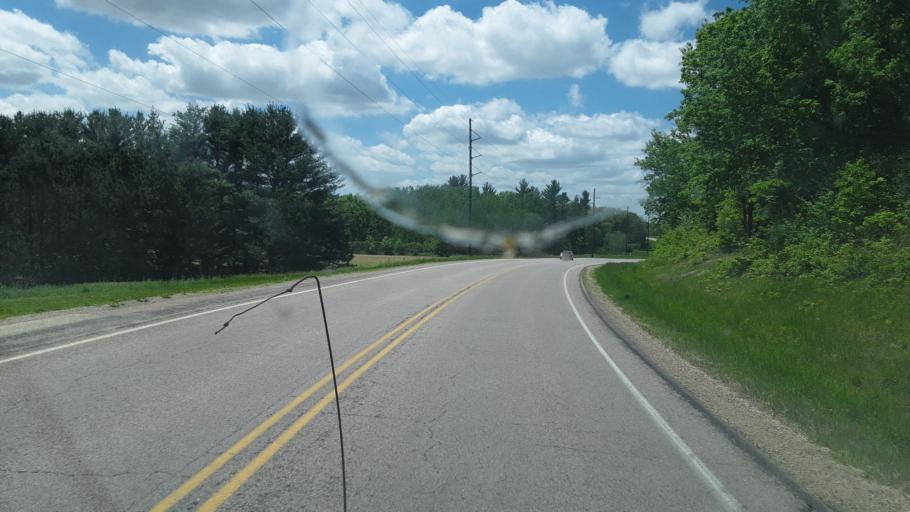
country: US
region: Wisconsin
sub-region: Sauk County
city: Lake Delton
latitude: 43.5901
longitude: -89.8937
